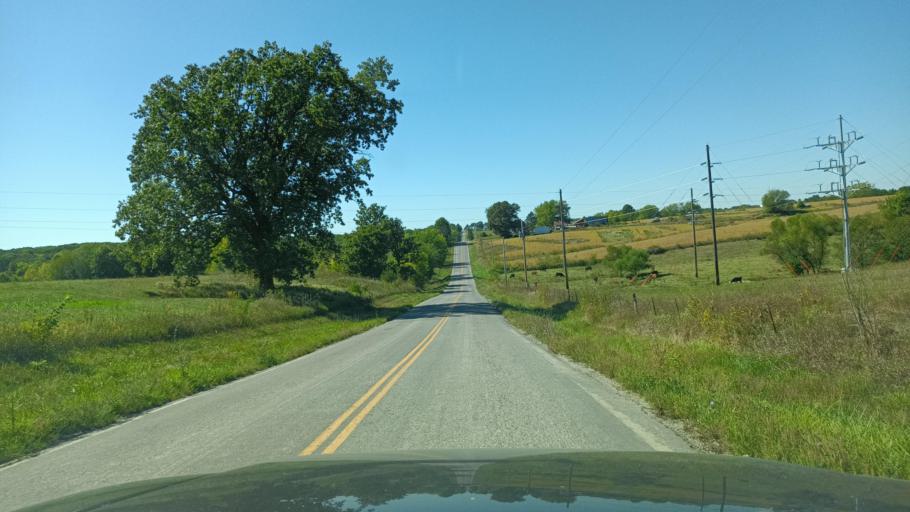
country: US
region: Missouri
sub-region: Macon County
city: La Plata
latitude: 40.0216
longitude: -92.5309
